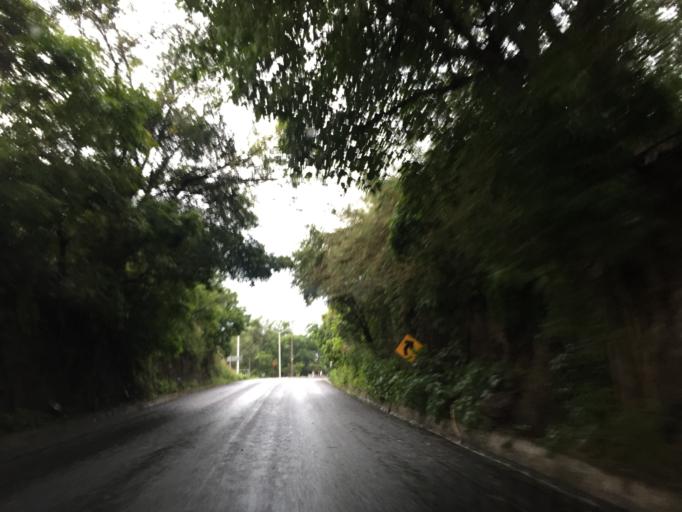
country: MX
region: Colima
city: Queseria
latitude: 19.3880
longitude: -103.5667
